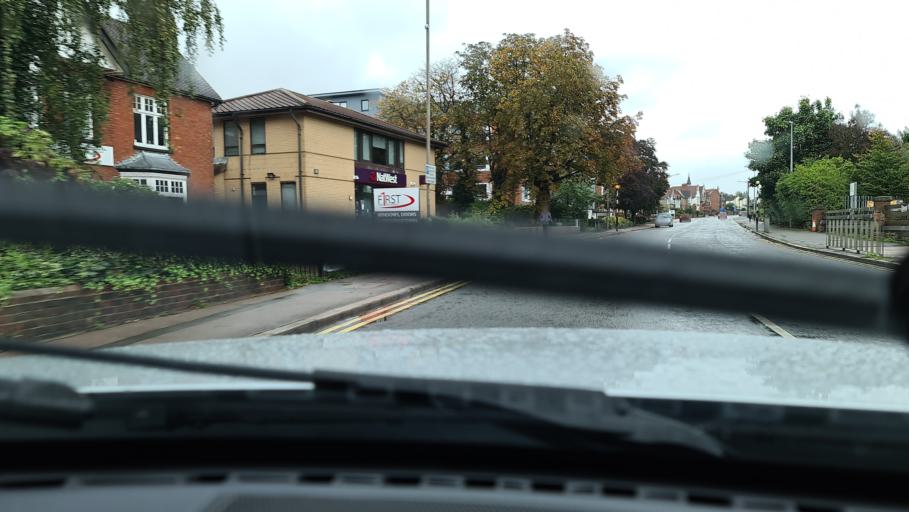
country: GB
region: England
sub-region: Buckinghamshire
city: Bletchley
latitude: 51.9957
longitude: -0.7256
